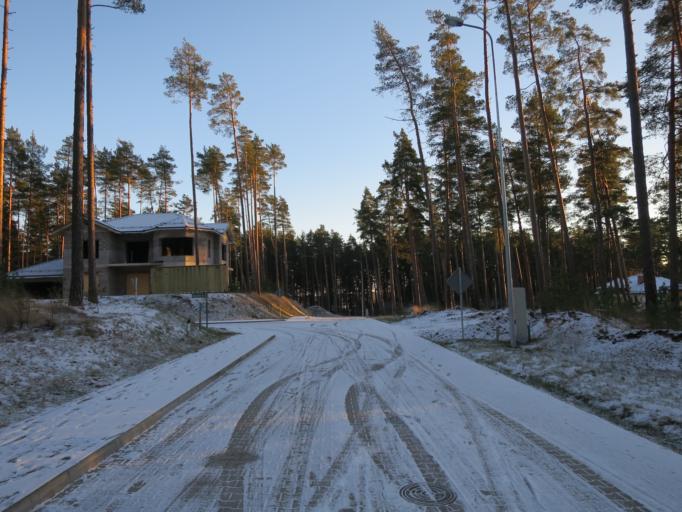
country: LV
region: Riga
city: Bergi
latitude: 56.9804
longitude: 24.3119
